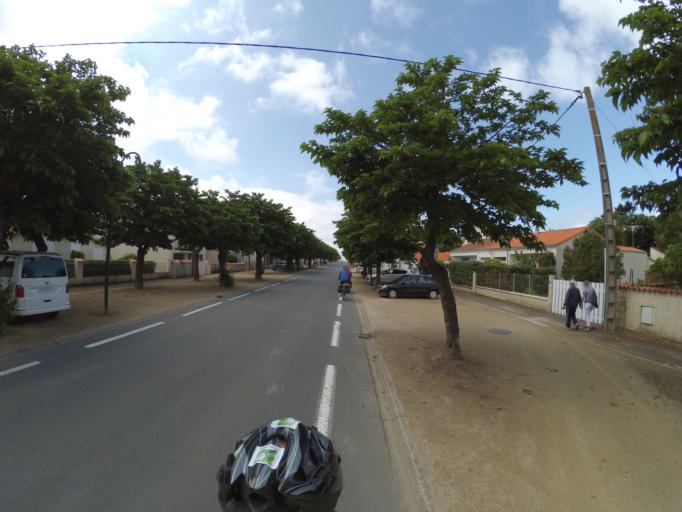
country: FR
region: Poitou-Charentes
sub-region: Departement de la Charente-Maritime
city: Chatelaillon-Plage
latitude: 46.0648
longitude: -1.0918
